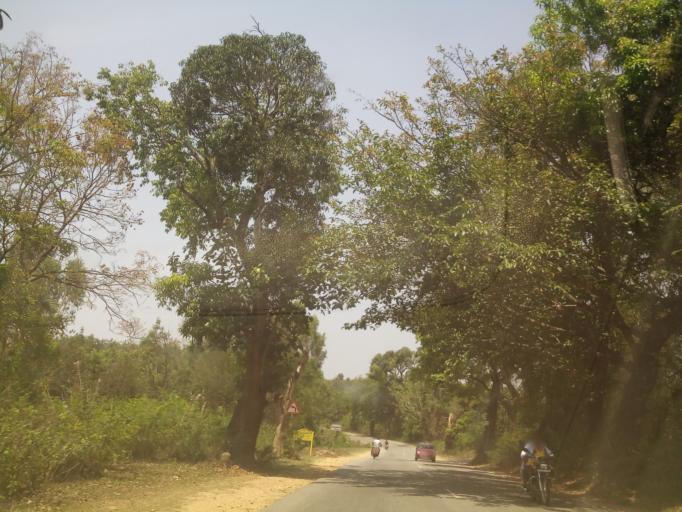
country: IN
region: Karnataka
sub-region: Hassan
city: Alur
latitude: 12.9551
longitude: 75.9197
